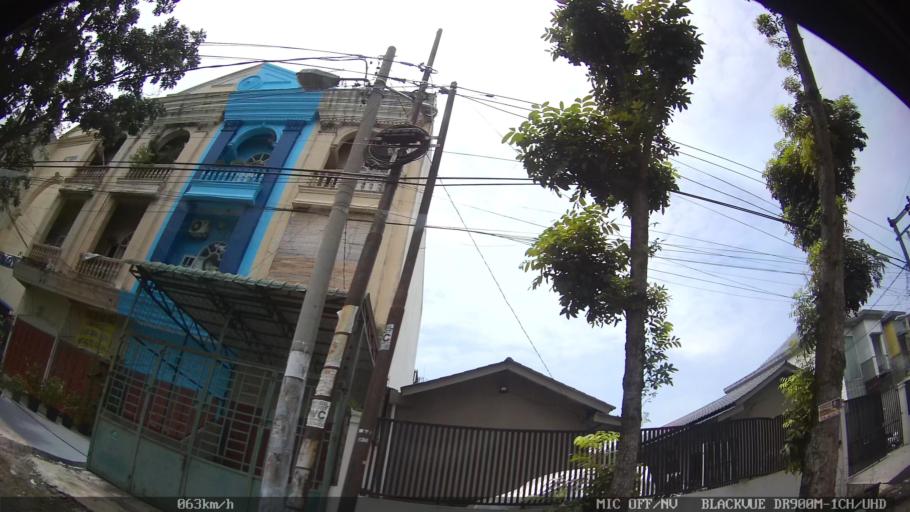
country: ID
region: North Sumatra
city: Sunggal
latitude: 3.5550
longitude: 98.6397
